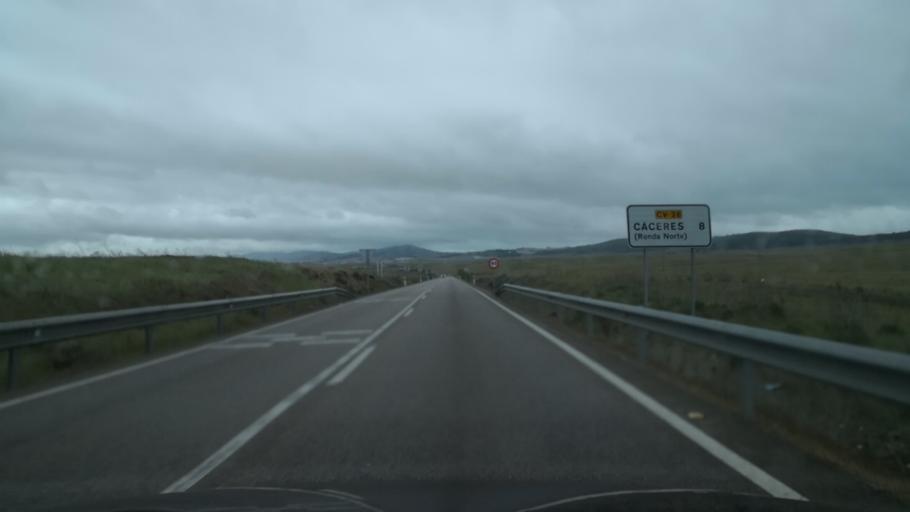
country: ES
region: Extremadura
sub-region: Provincia de Caceres
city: Casar de Caceres
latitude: 39.5346
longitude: -6.4061
